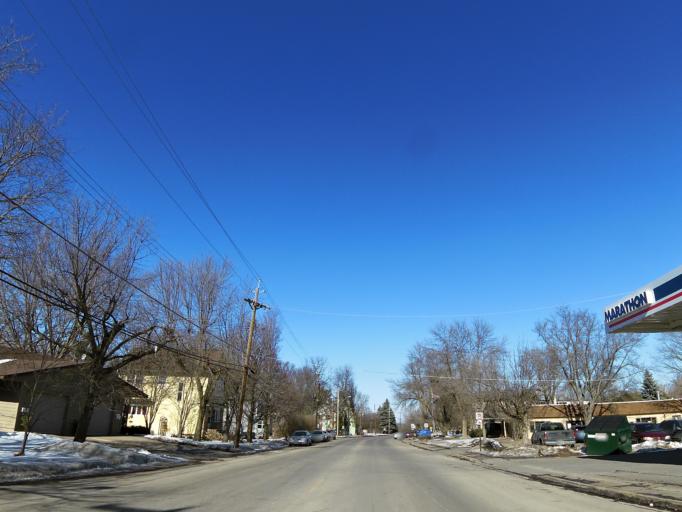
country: US
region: Minnesota
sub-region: Washington County
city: Stillwater
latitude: 45.0648
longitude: -92.8205
